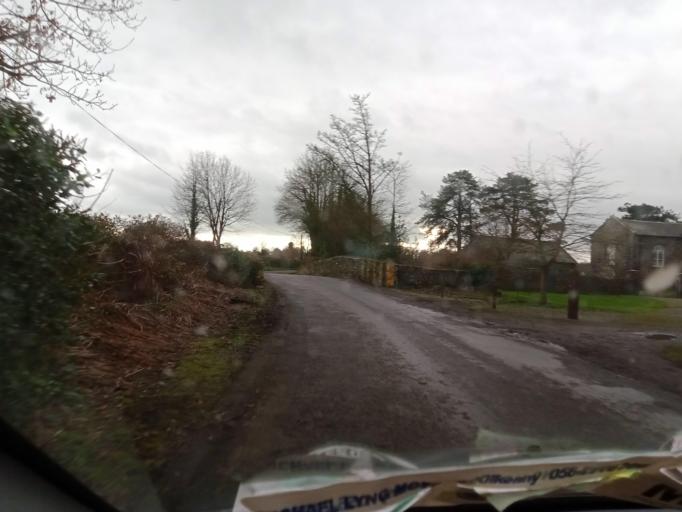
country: IE
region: Munster
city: Fethard
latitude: 52.5181
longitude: -7.7560
